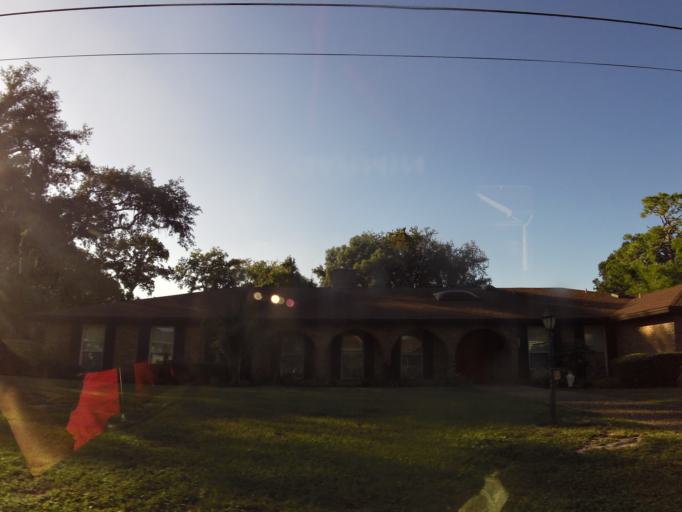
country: US
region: Florida
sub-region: Duval County
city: Jacksonville
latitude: 30.2528
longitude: -81.6358
